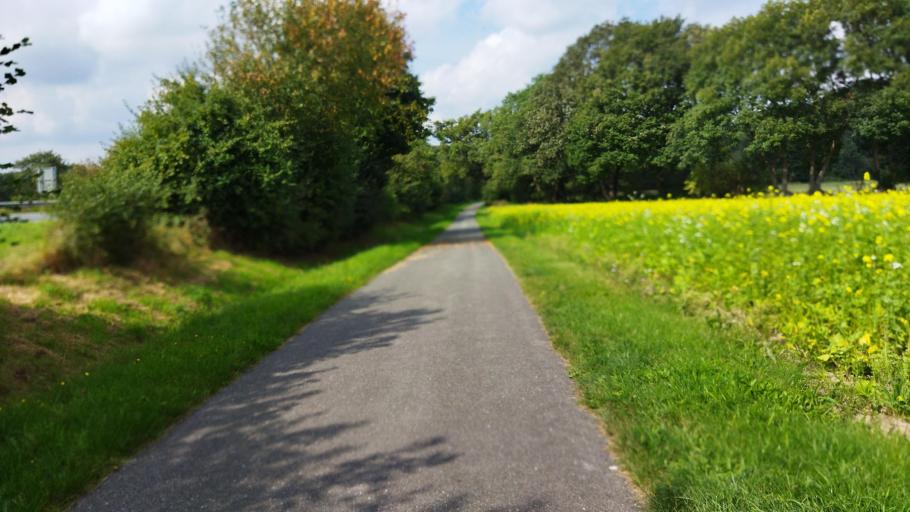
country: DE
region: North Rhine-Westphalia
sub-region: Regierungsbezirk Munster
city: Telgte
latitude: 51.9697
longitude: 7.8285
